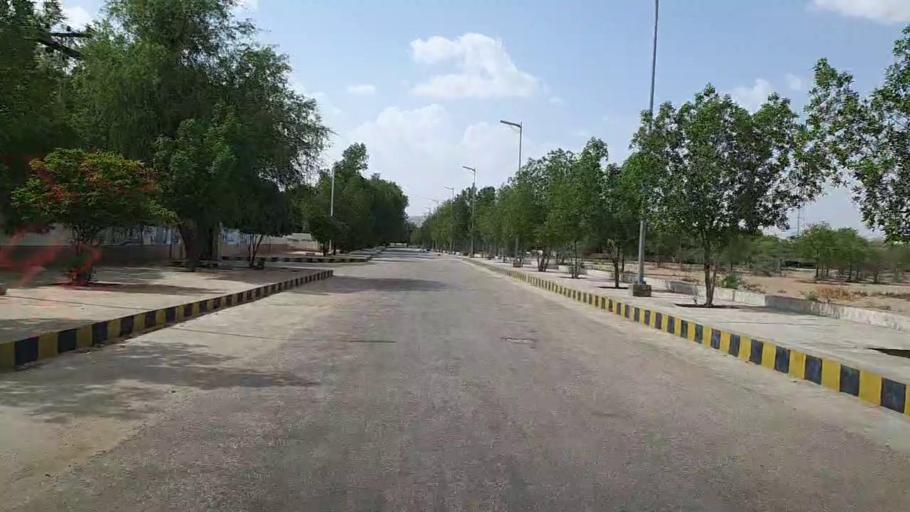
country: PK
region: Sindh
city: Jamshoro
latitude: 25.4047
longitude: 67.7856
